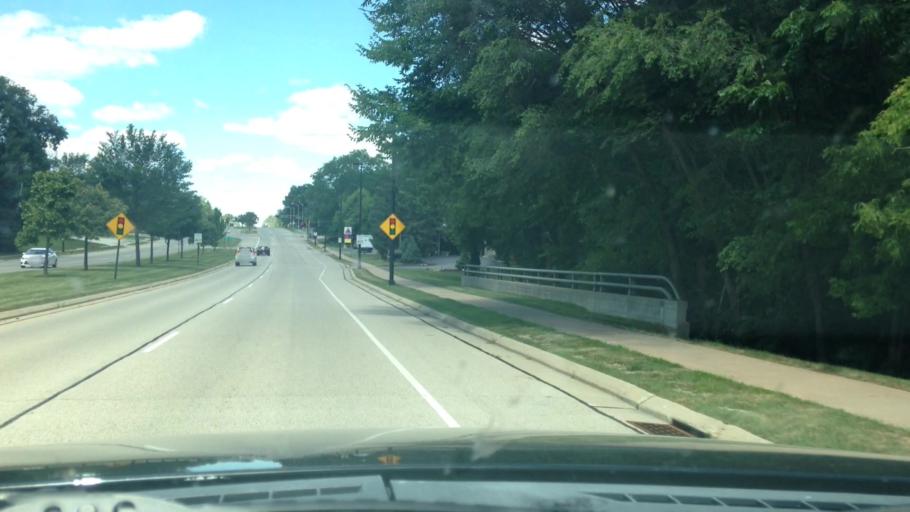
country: US
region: Wisconsin
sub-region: Waukesha County
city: Menomonee Falls
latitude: 43.1538
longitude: -88.0817
